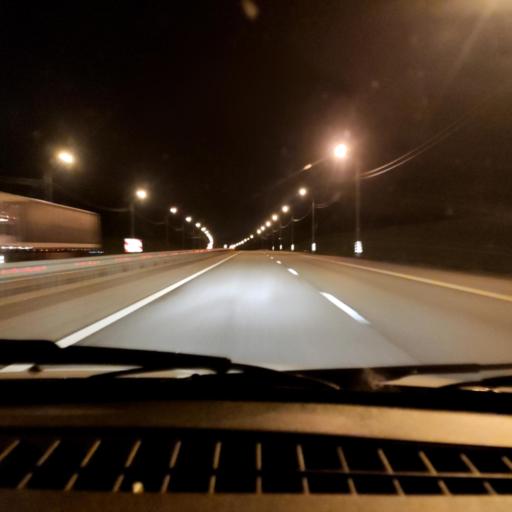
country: RU
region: Lipetsk
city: Zadonsk
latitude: 52.3592
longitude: 38.9389
